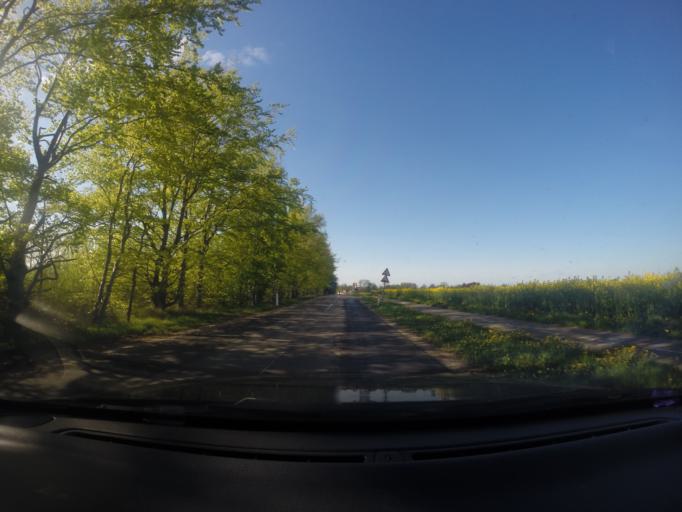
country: DK
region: Capital Region
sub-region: Hoje-Taastrup Kommune
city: Taastrup
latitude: 55.6764
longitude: 12.2533
